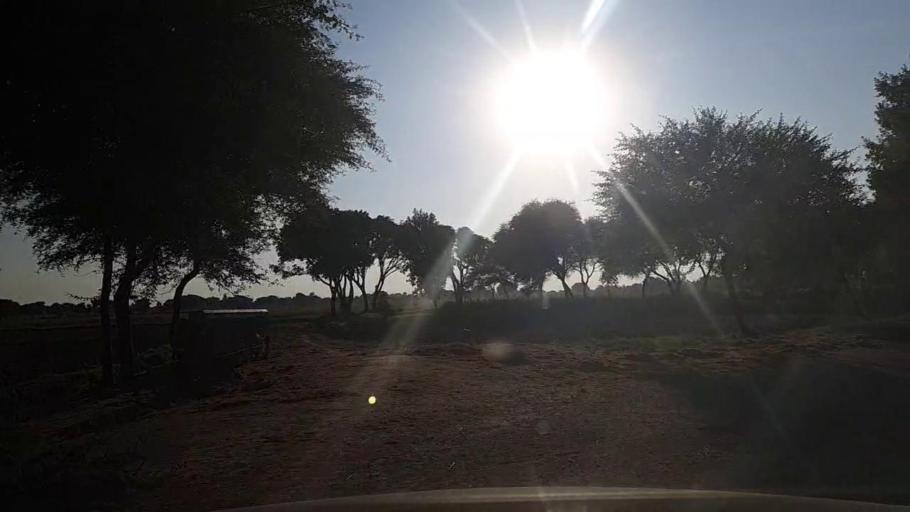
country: PK
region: Sindh
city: Mirpur Batoro
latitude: 24.7068
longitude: 68.3209
